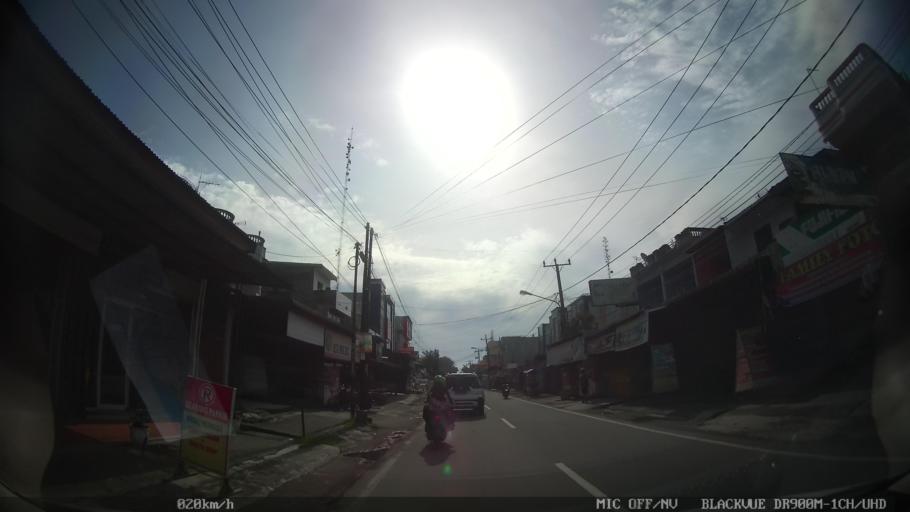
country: ID
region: North Sumatra
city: Medan
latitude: 3.6102
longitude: 98.6429
